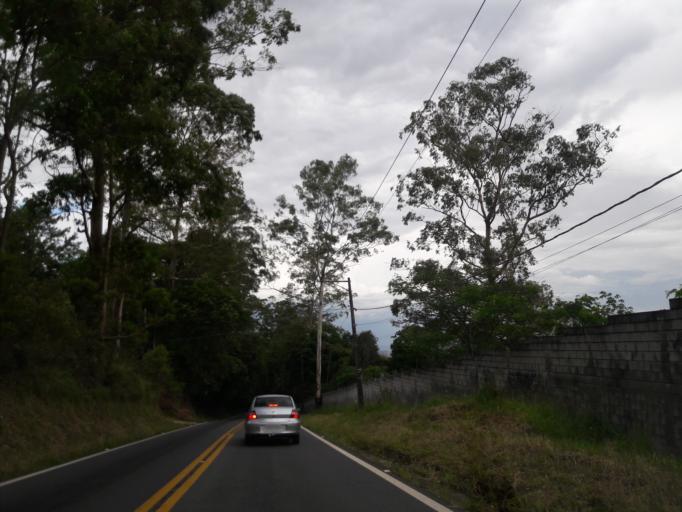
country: BR
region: Sao Paulo
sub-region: Aruja
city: Aruja
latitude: -23.3496
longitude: -46.4240
